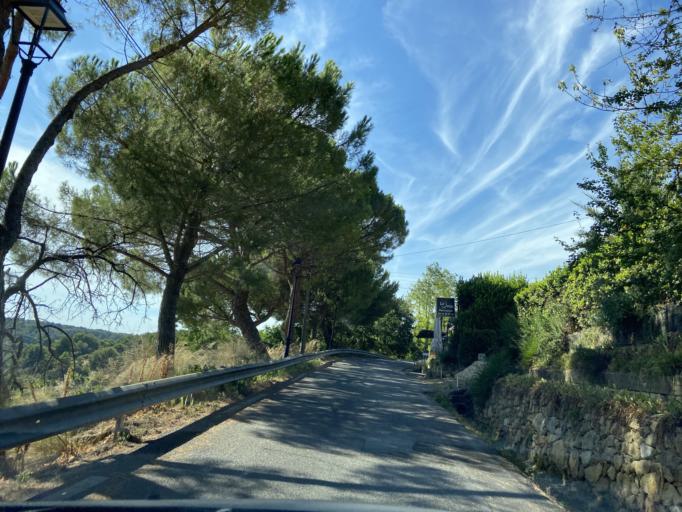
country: FR
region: Provence-Alpes-Cote d'Azur
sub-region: Departement des Bouches-du-Rhone
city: Saint-Chamas
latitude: 43.5627
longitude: 5.0236
